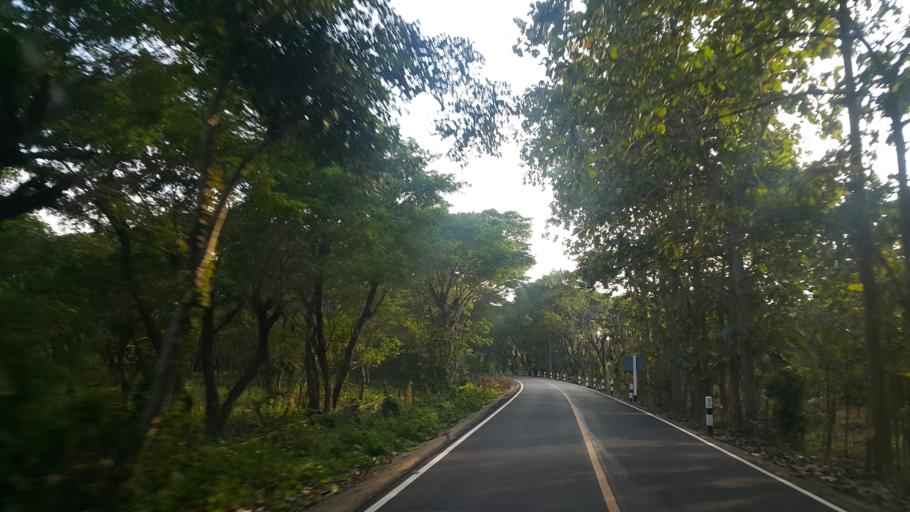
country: TH
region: Lampang
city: Sop Prap
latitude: 17.9375
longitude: 99.3407
